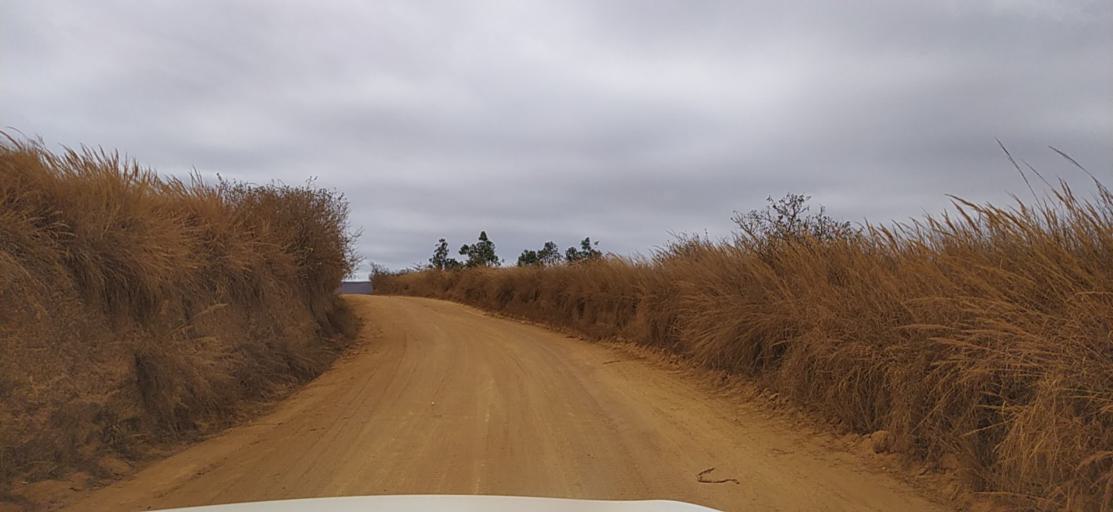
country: MG
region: Alaotra Mangoro
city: Ambatondrazaka
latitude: -17.9128
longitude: 48.2647
